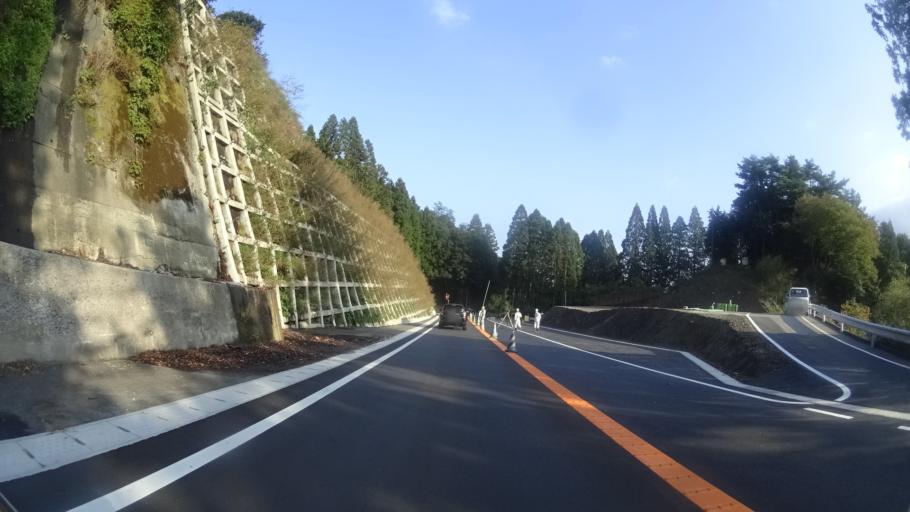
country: JP
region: Oita
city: Beppu
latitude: 33.2704
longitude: 131.4345
